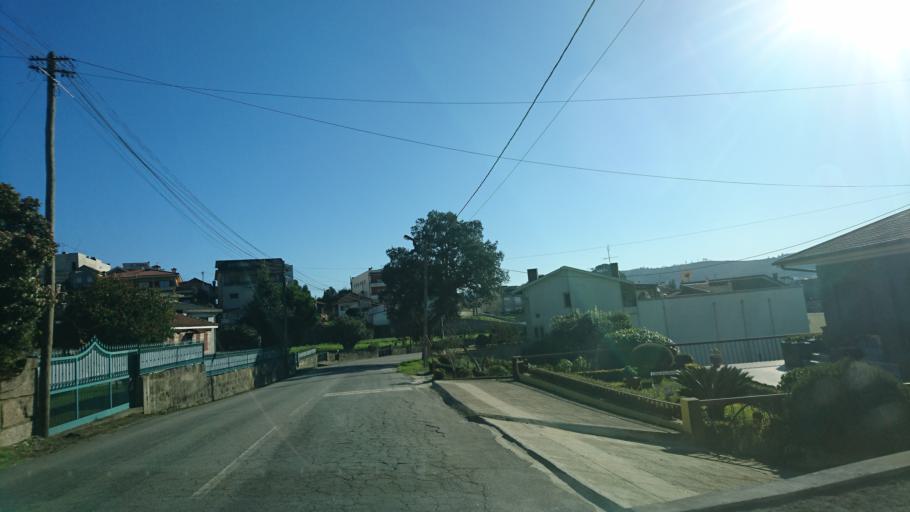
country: PT
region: Porto
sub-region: Paredes
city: Recarei
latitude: 41.1549
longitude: -8.3963
